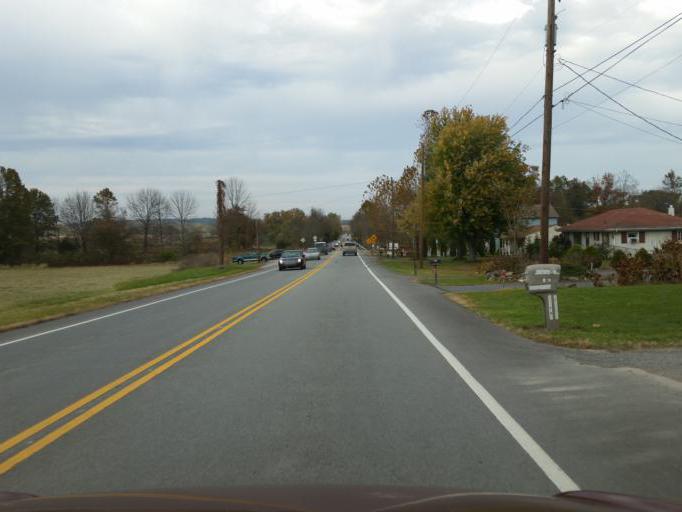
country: US
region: Pennsylvania
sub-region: Lancaster County
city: Elizabethtown
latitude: 40.1855
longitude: -76.6015
